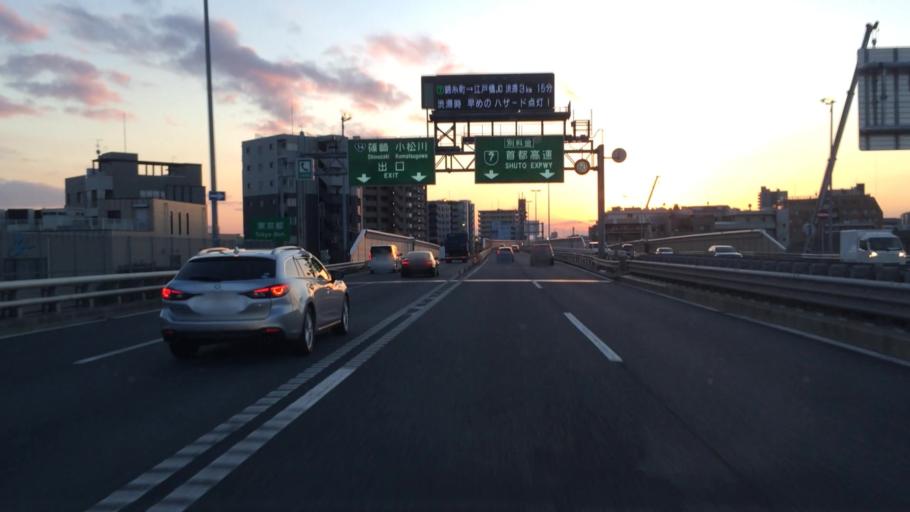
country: JP
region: Tokyo
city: Urayasu
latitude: 35.7074
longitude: 139.9128
